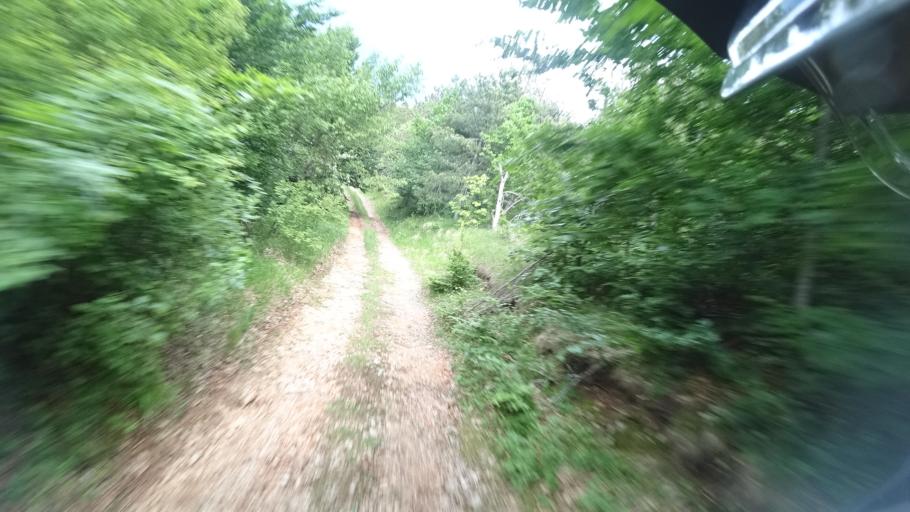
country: HR
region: Zadarska
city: Obrovac
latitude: 44.2724
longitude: 15.7408
